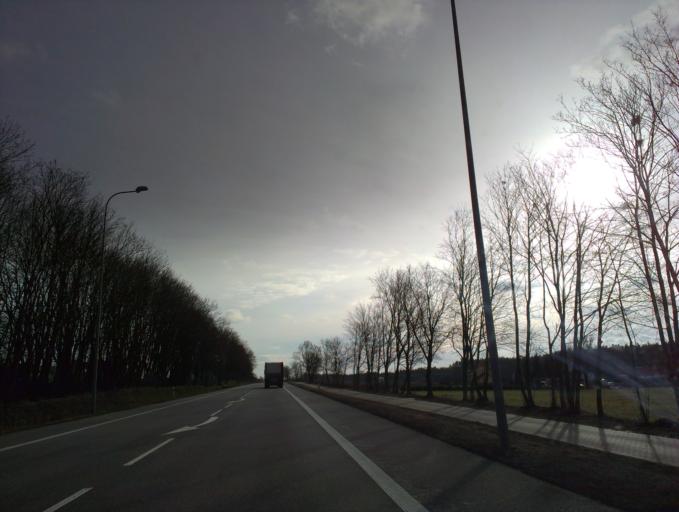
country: PL
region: Kujawsko-Pomorskie
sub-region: Powiat lipnowski
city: Lipno
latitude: 52.8686
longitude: 19.1536
